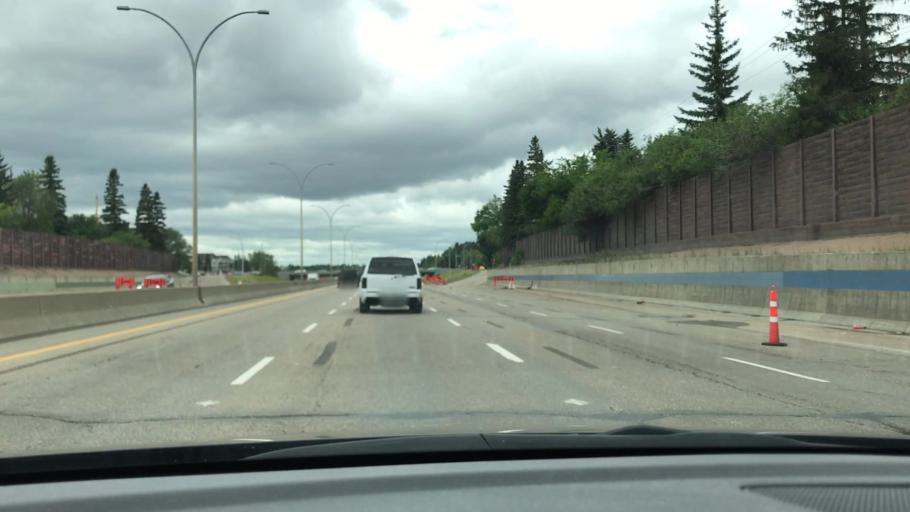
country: CA
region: Alberta
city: Edmonton
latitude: 53.4832
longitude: -113.5357
